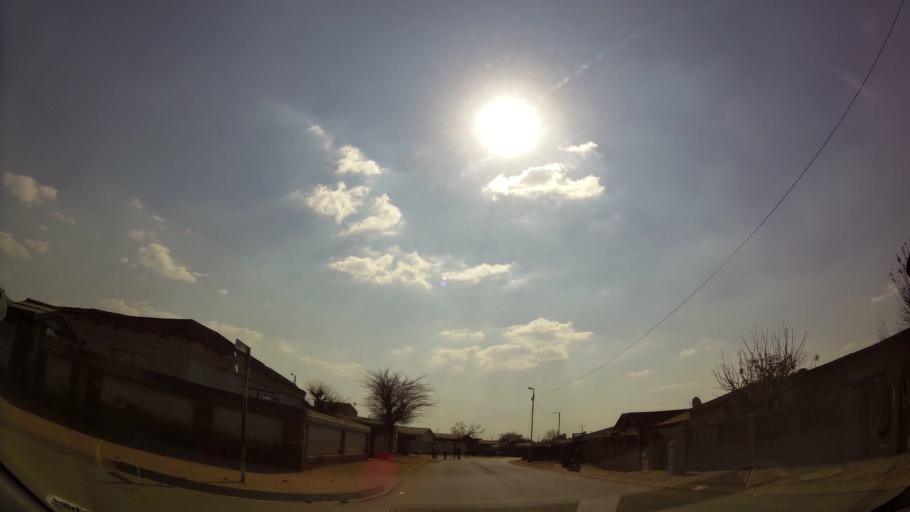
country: ZA
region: Gauteng
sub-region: Ekurhuleni Metropolitan Municipality
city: Brakpan
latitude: -26.1511
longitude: 28.4126
